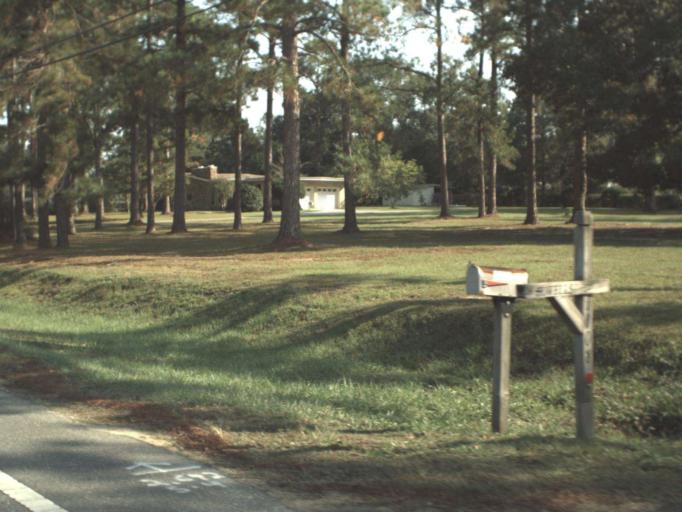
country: US
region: Florida
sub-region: Holmes County
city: Bonifay
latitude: 30.7818
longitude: -85.6800
